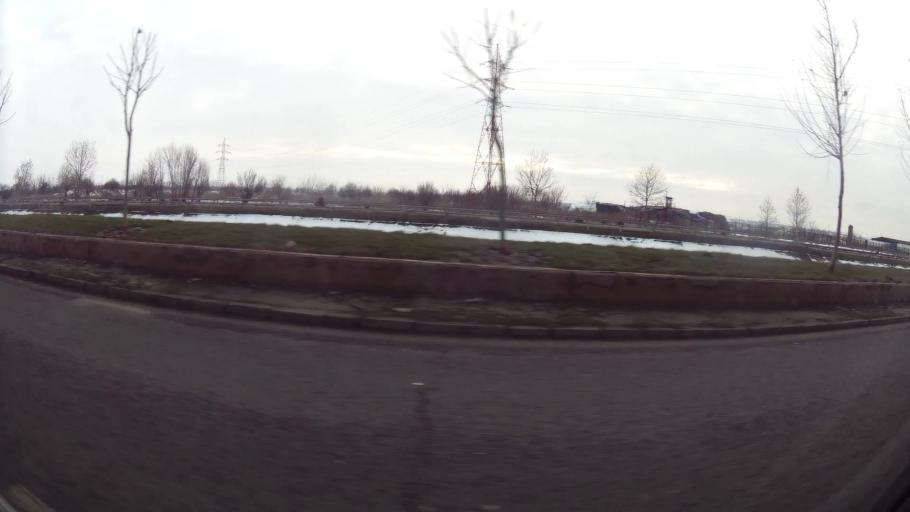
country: RO
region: Ilfov
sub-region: Comuna Popesti-Leordeni
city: Popesti-Leordeni
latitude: 44.3952
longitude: 26.1762
